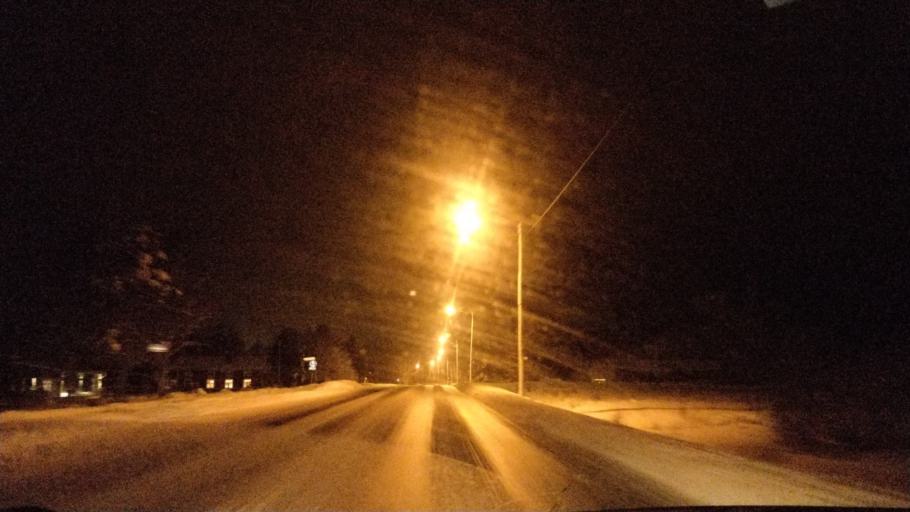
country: FI
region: Lapland
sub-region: Rovaniemi
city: Rovaniemi
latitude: 66.3947
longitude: 25.3828
